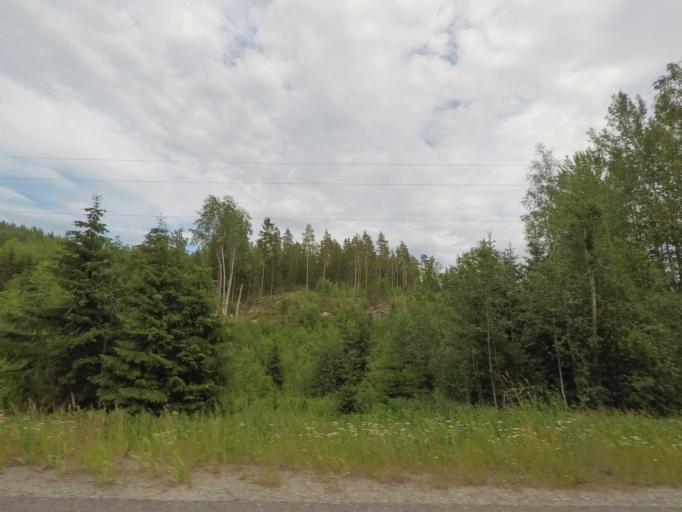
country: FI
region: Paijanne Tavastia
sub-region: Lahti
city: Hollola
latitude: 60.8954
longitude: 25.5232
